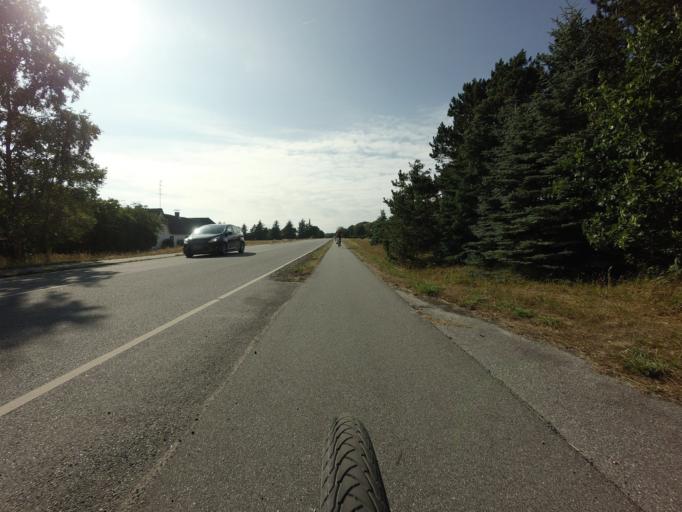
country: DK
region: North Denmark
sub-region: Laeso Kommune
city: Byrum
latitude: 57.2739
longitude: 10.9473
